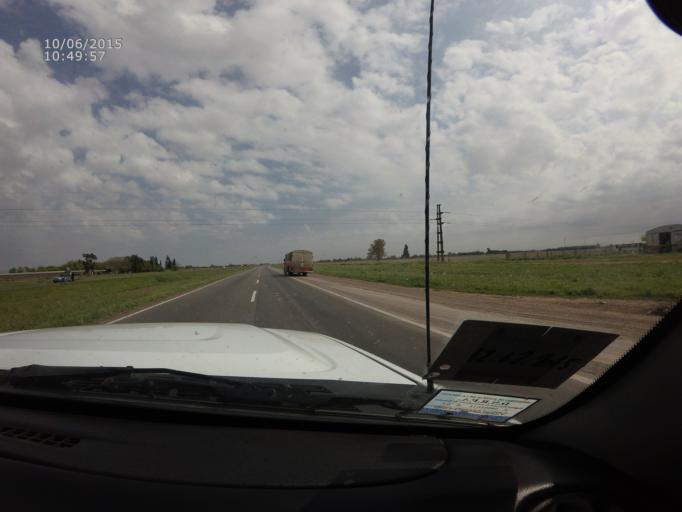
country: AR
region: Buenos Aires
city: San Nicolas de los Arroyos
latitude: -33.3799
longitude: -60.2339
